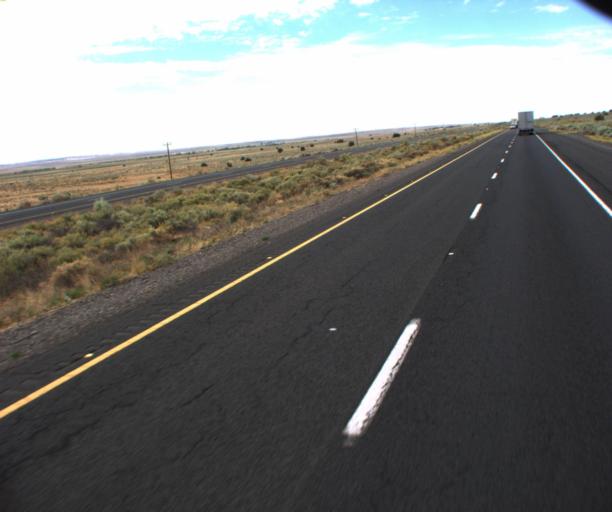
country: US
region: Arizona
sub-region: Apache County
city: Houck
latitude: 35.1495
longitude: -109.5095
